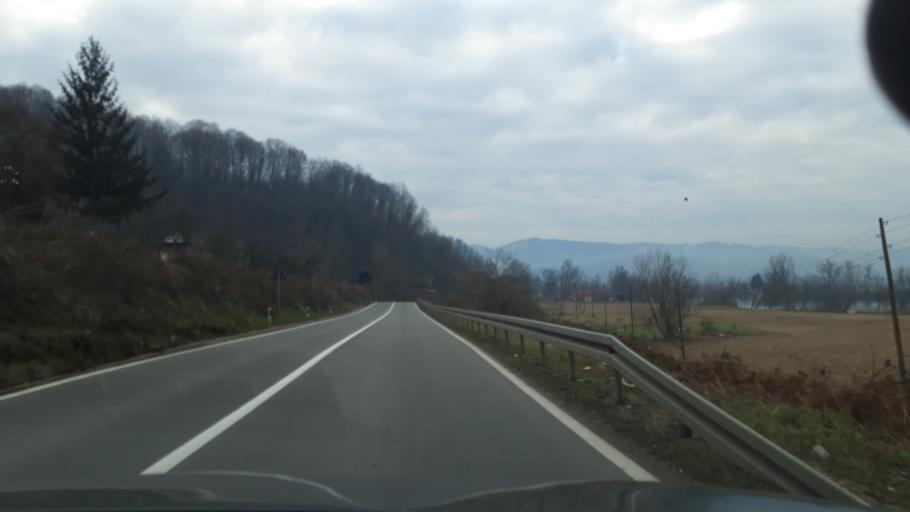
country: BA
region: Republika Srpska
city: Zvornik
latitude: 44.4263
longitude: 19.1505
